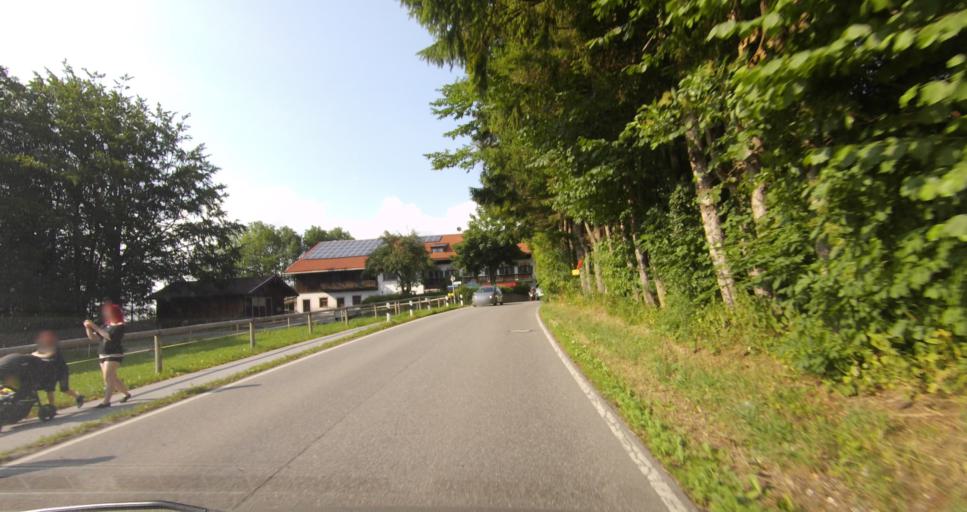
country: DE
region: Bavaria
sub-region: Upper Bavaria
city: Fischbachau
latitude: 47.7246
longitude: 11.9518
